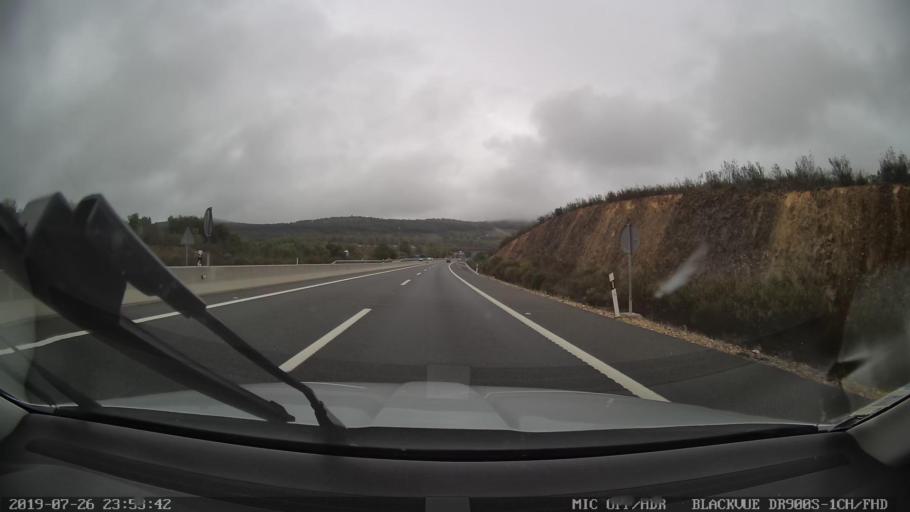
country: ES
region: Extremadura
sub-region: Provincia de Caceres
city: Casas de Miravete
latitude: 39.6850
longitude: -5.7200
